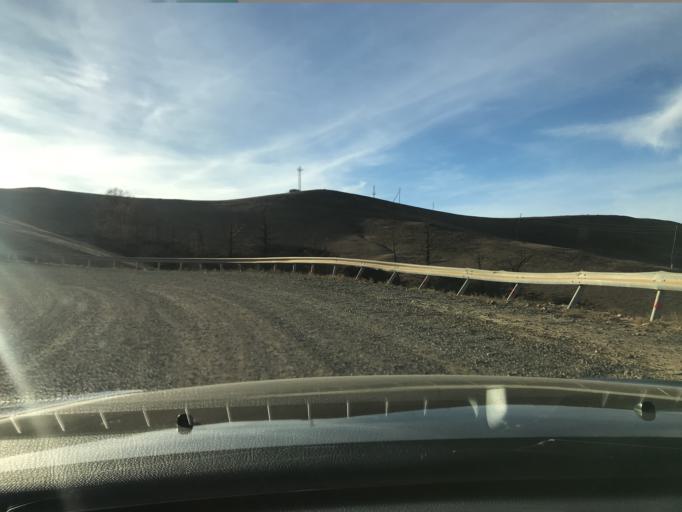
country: MN
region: Central Aimak
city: Dzuunmod
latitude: 47.8143
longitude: 107.3270
